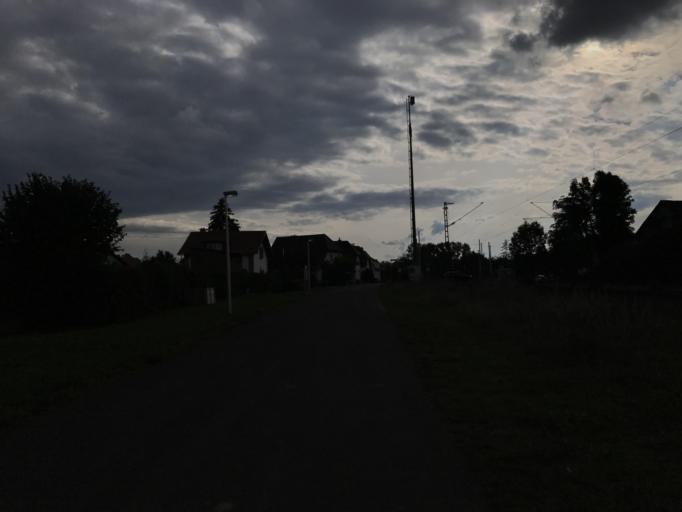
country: DE
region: Hesse
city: Borken
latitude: 51.0597
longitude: 9.3252
